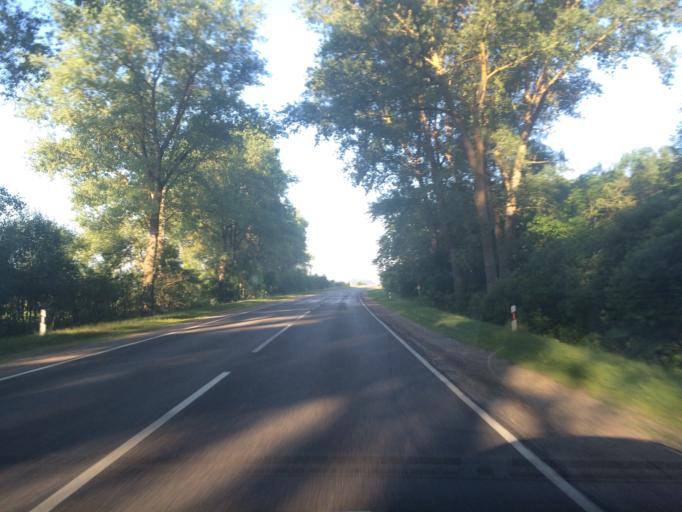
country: LT
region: Utenos apskritis
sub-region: Anyksciai
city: Anyksciai
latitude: 55.3681
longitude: 25.0081
